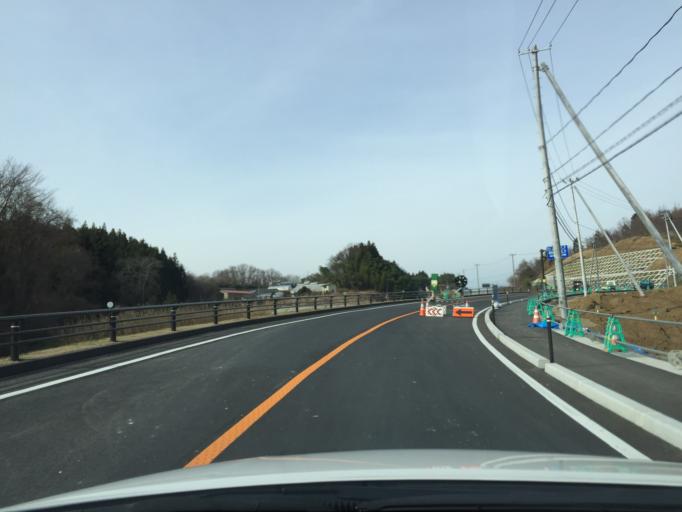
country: JP
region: Fukushima
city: Funehikimachi-funehiki
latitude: 37.4383
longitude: 140.5417
